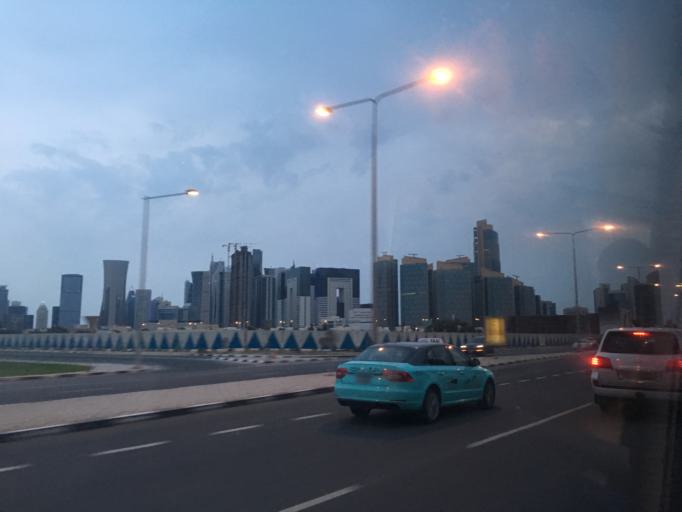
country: QA
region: Baladiyat ad Dawhah
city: Doha
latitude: 25.3226
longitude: 51.5105
